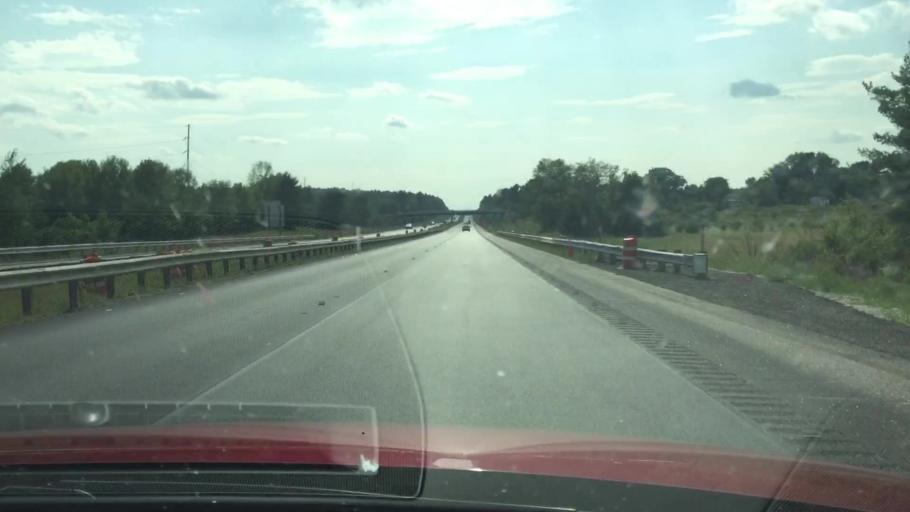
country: US
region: Maine
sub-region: Androscoggin County
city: Auburn
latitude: 44.0550
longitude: -70.2214
